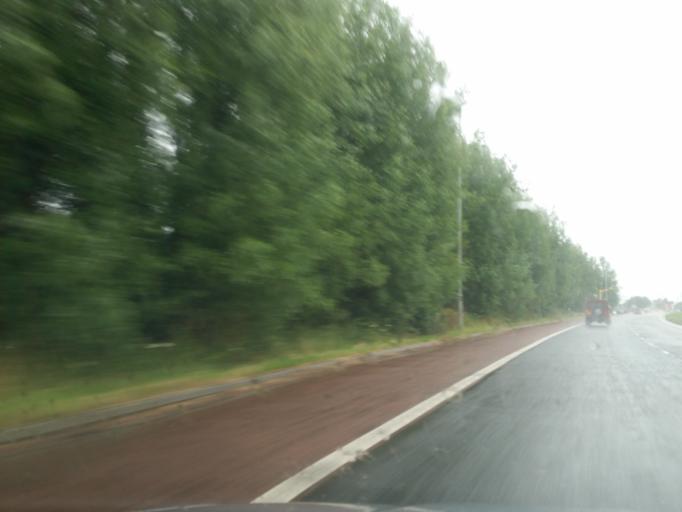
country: GB
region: Northern Ireland
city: Holywood
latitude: 54.6390
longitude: -5.8417
